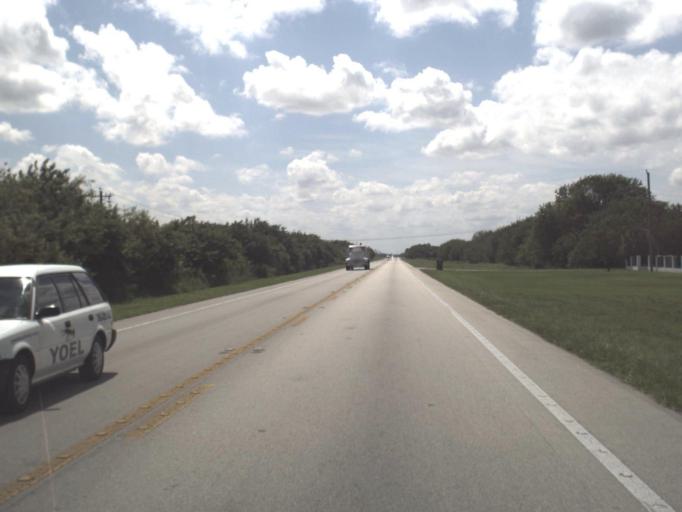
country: US
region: Florida
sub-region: Collier County
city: Immokalee
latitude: 26.4829
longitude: -81.4346
